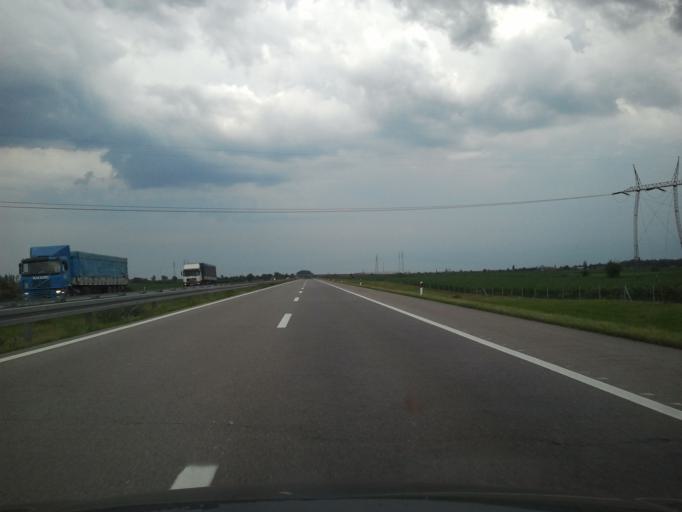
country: RS
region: Autonomna Pokrajina Vojvodina
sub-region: Sremski Okrug
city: Sremska Mitrovica
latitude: 45.0099
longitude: 19.5907
